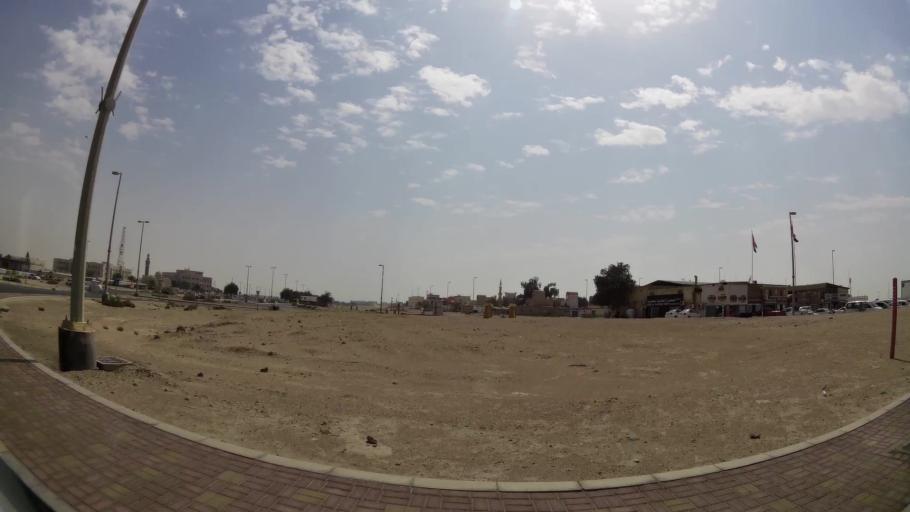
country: AE
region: Abu Dhabi
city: Abu Dhabi
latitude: 24.3159
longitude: 54.6068
